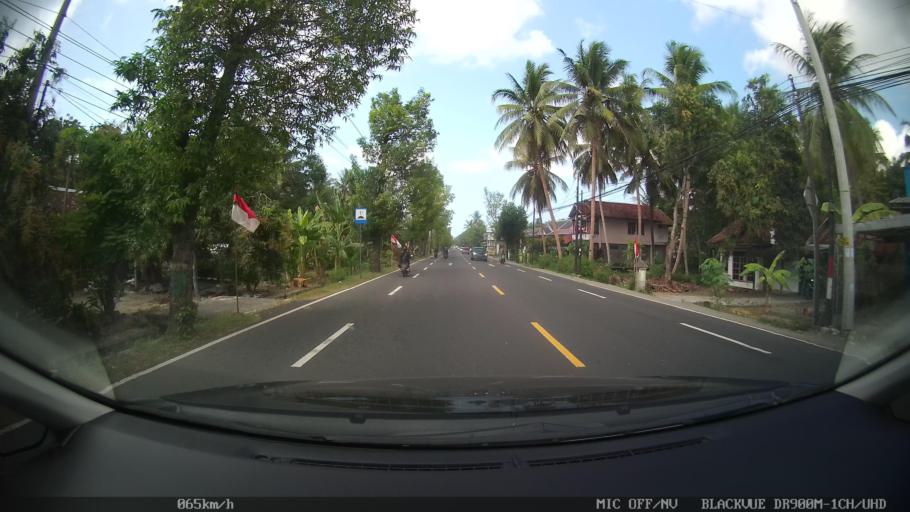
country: ID
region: Daerah Istimewa Yogyakarta
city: Srandakan
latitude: -7.8798
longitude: 110.1323
